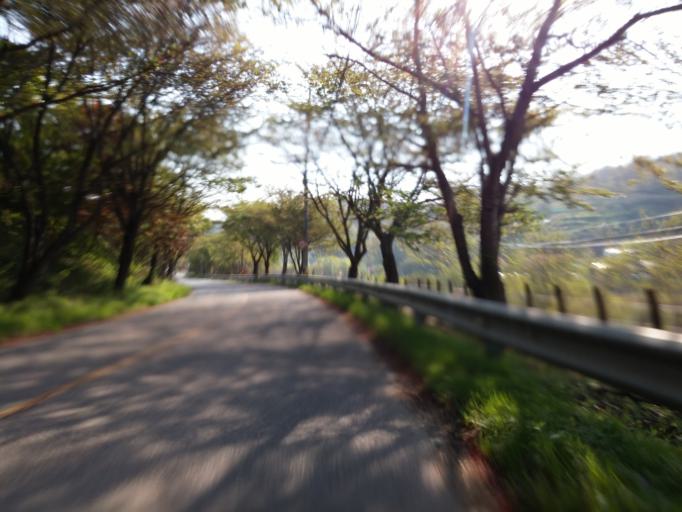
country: KR
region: Daejeon
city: Sintansin
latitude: 36.4379
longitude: 127.4660
